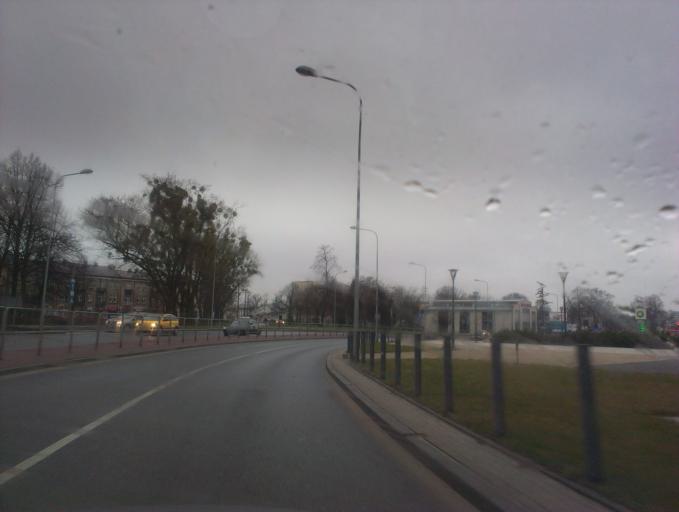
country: PL
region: Masovian Voivodeship
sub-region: Radom
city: Radom
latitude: 51.4049
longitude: 21.1544
